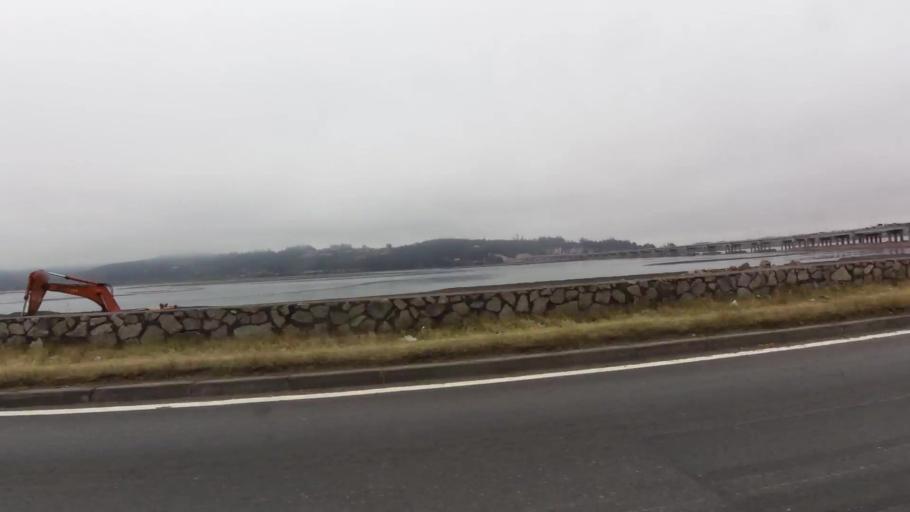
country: CL
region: Biobio
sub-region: Provincia de Concepcion
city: Concepcion
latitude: -36.8380
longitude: -73.0611
